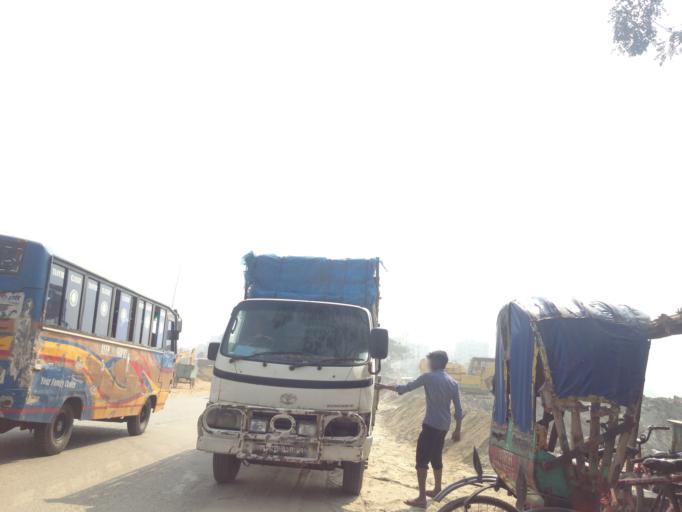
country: BD
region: Dhaka
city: Azimpur
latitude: 23.8059
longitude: 90.3427
